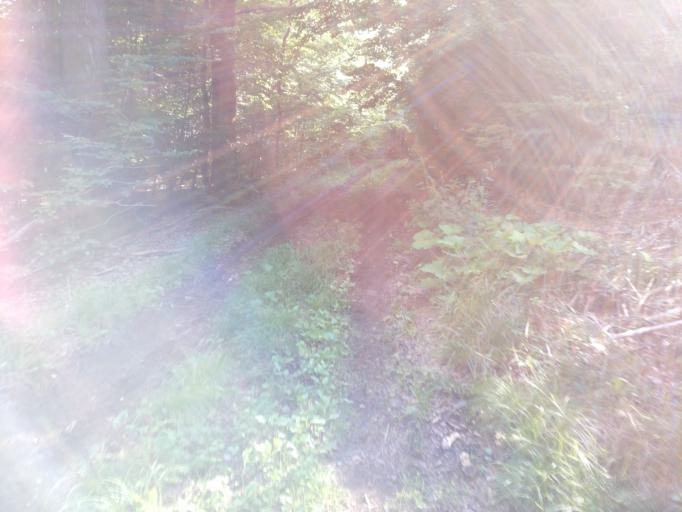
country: DE
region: Hesse
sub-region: Regierungsbezirk Giessen
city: Greifenstein
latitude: 50.6176
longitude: 8.2851
